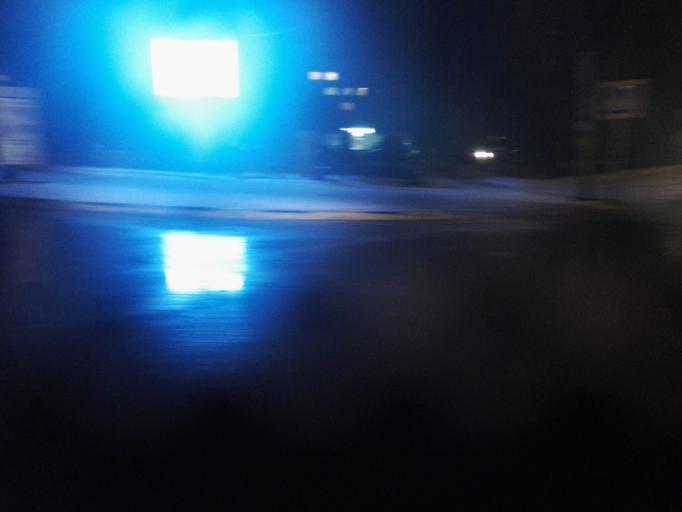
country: RU
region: Tula
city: Novomoskovsk
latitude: 54.0108
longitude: 38.2735
